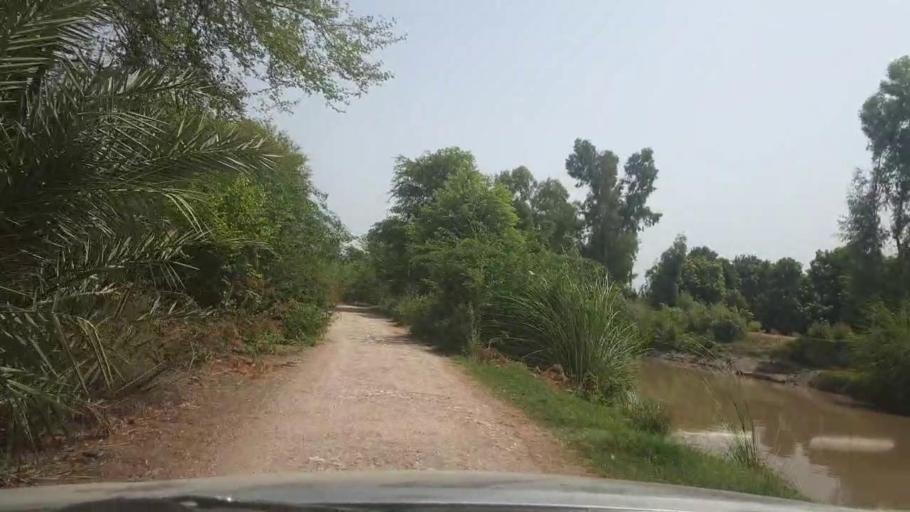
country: PK
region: Sindh
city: Pano Aqil
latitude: 27.8995
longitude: 69.1459
